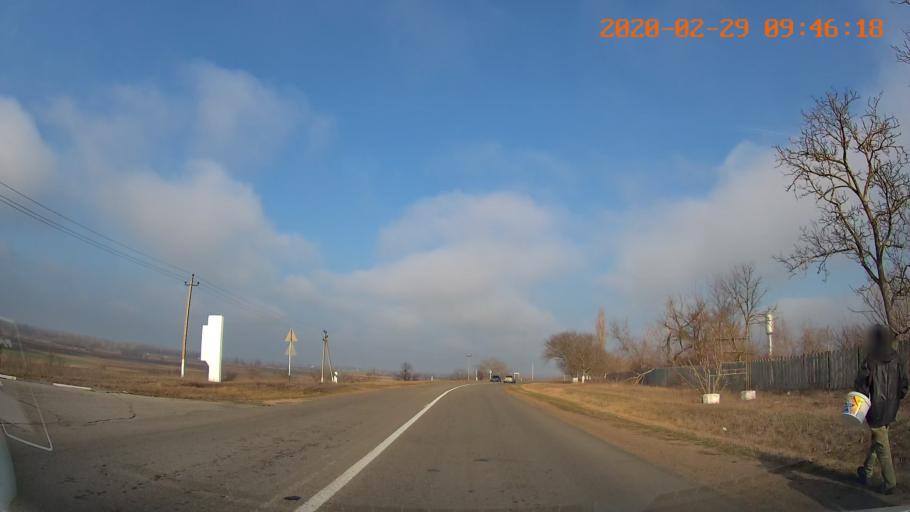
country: MD
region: Telenesti
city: Crasnoe
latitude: 46.6656
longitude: 29.7999
